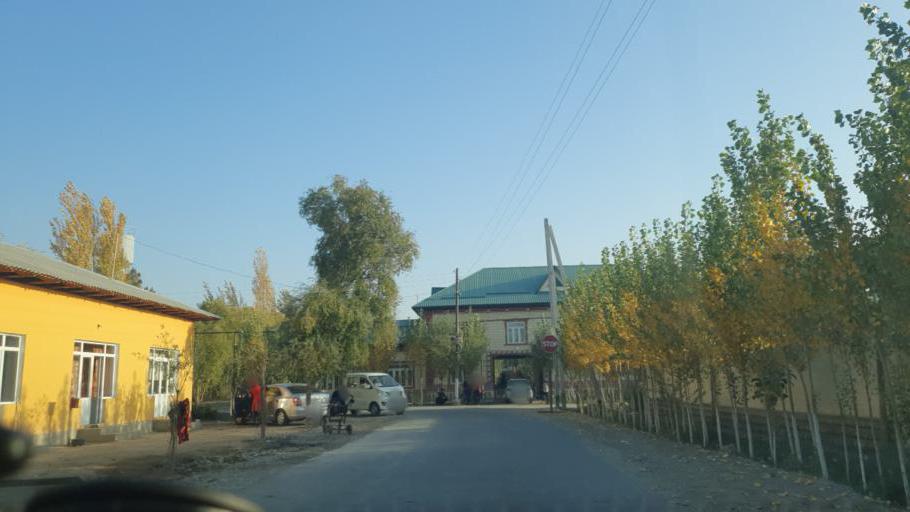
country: UZ
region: Fergana
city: Beshariq
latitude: 40.4623
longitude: 70.5438
